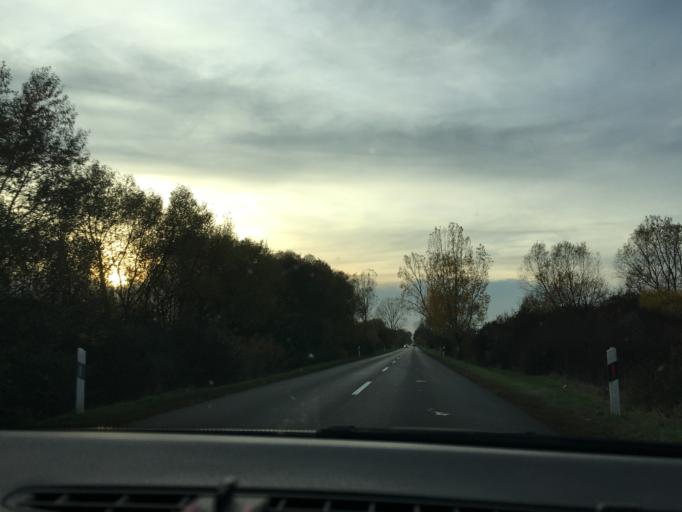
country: HU
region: Szabolcs-Szatmar-Bereg
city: Kisleta
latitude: 47.8544
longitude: 21.9986
